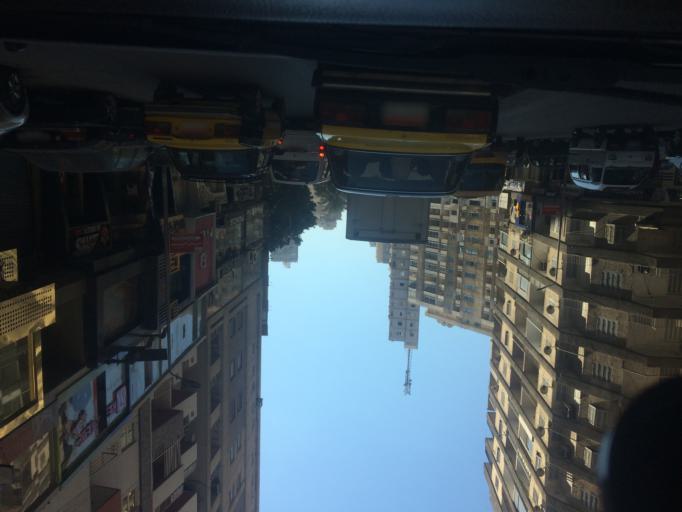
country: EG
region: Alexandria
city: Alexandria
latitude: 31.2629
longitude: 29.9944
